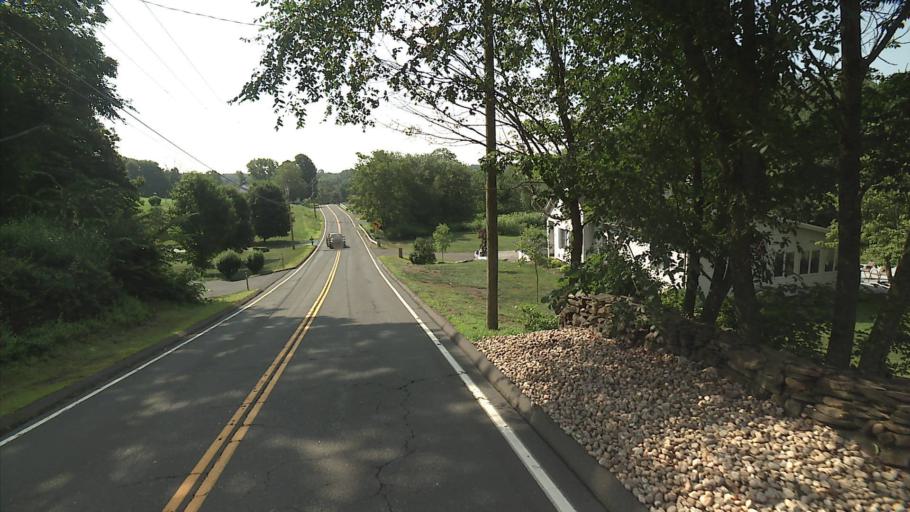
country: US
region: Connecticut
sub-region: New Haven County
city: Wolcott
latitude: 41.5988
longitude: -72.9660
